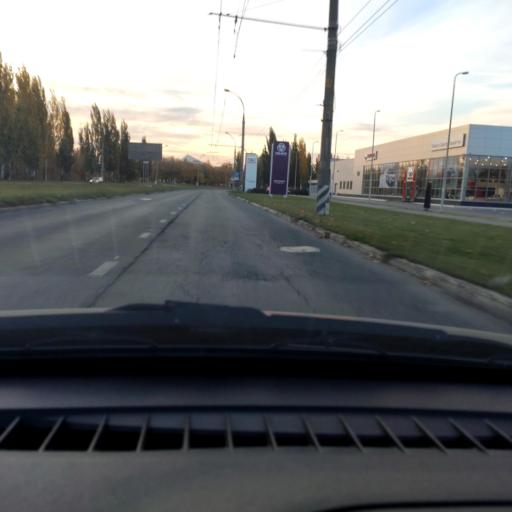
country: RU
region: Samara
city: Tol'yatti
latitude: 53.5450
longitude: 49.2769
